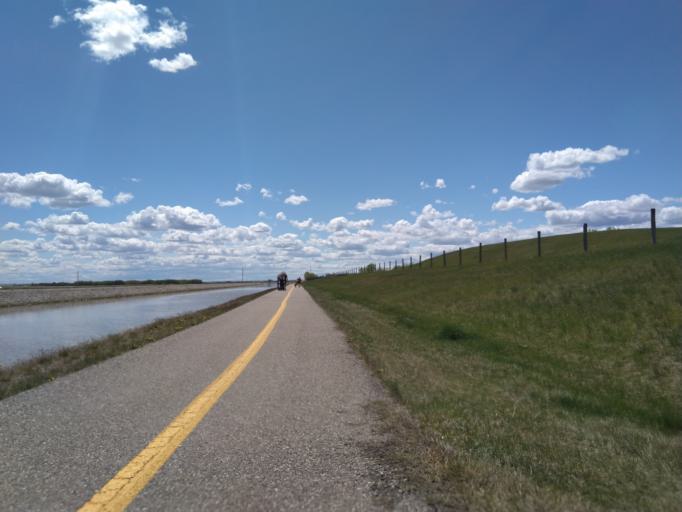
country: CA
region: Alberta
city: Chestermere
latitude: 51.0139
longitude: -113.8444
